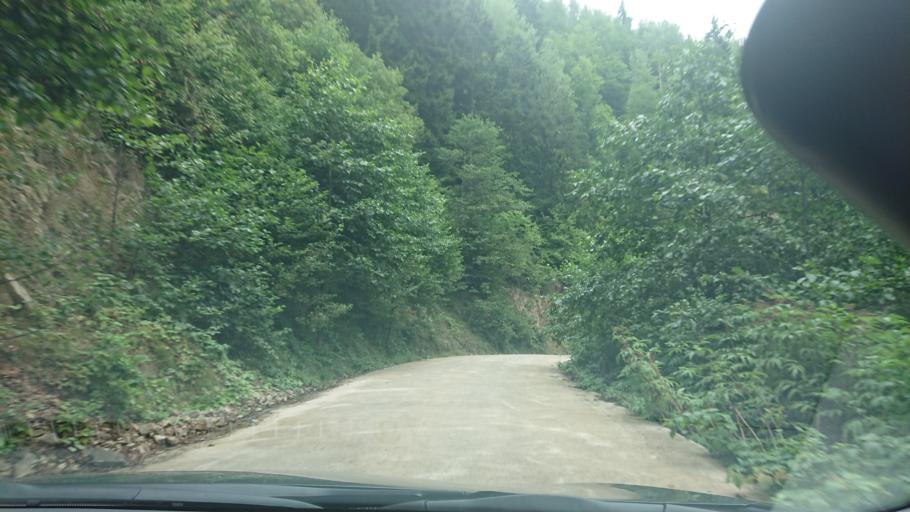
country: TR
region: Gumushane
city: Kurtun
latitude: 40.6705
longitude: 39.0392
